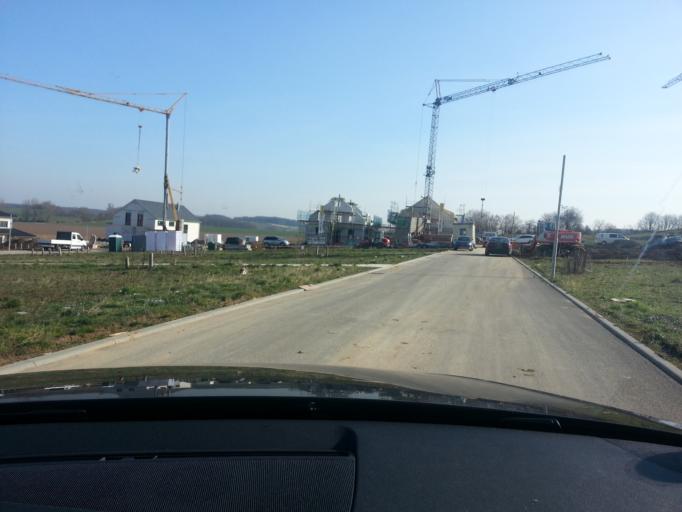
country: DE
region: Baden-Wuerttemberg
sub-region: Regierungsbezirk Stuttgart
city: Oedheim
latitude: 49.2109
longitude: 9.2631
